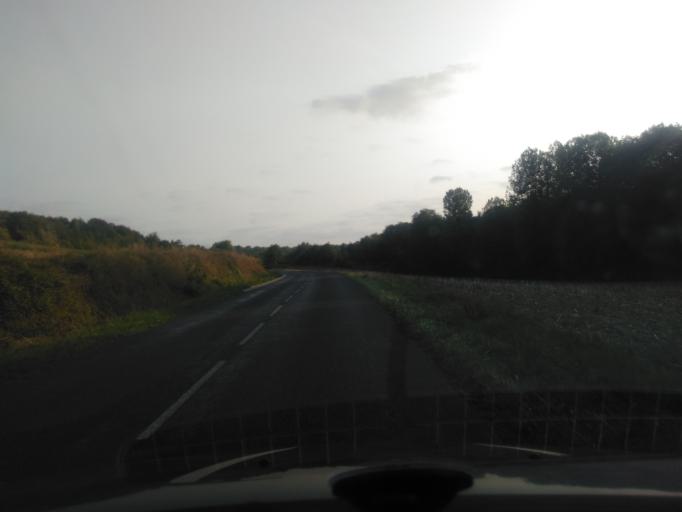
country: FR
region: Champagne-Ardenne
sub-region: Departement de la Marne
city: Fismes
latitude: 49.2540
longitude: 3.6969
